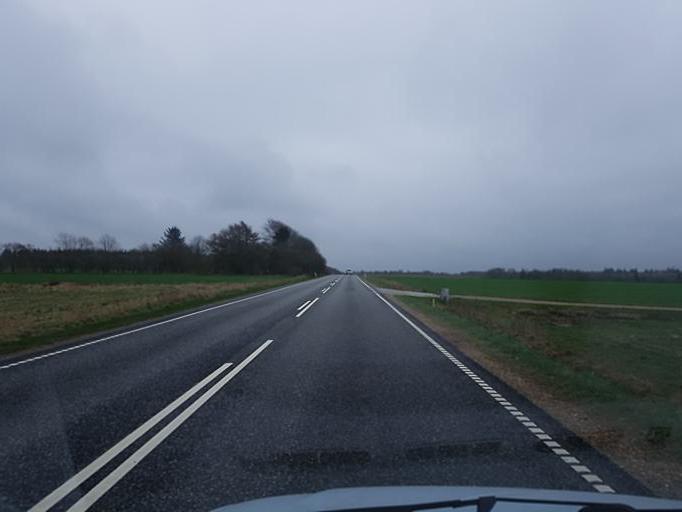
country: DK
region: Central Jutland
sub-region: Ringkobing-Skjern Kommune
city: Skjern
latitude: 56.0152
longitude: 8.4294
